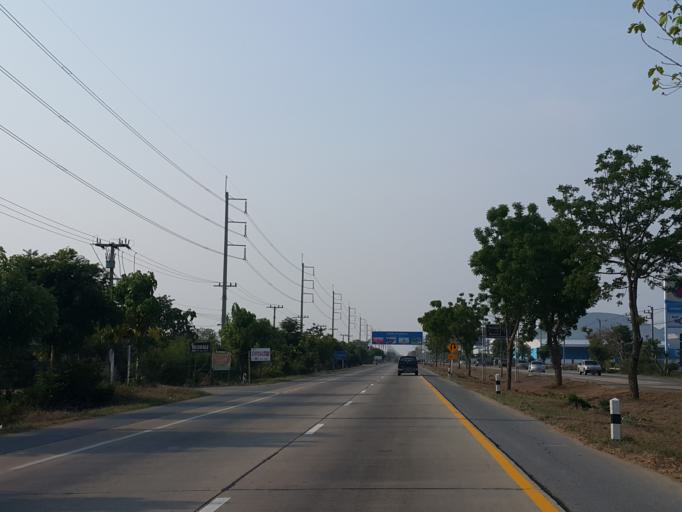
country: TH
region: Chai Nat
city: Hankha
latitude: 14.9485
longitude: 100.0816
